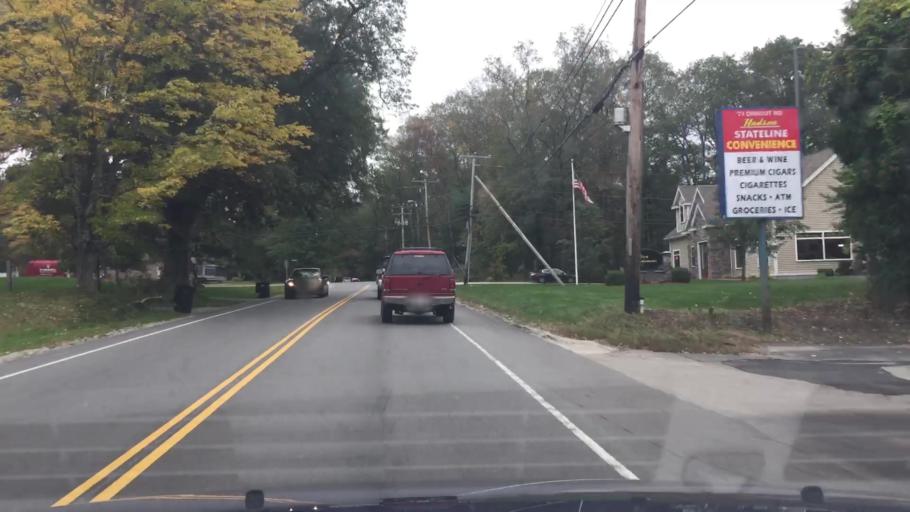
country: US
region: Massachusetts
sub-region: Middlesex County
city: Tyngsboro
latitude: 42.7101
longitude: -71.4052
